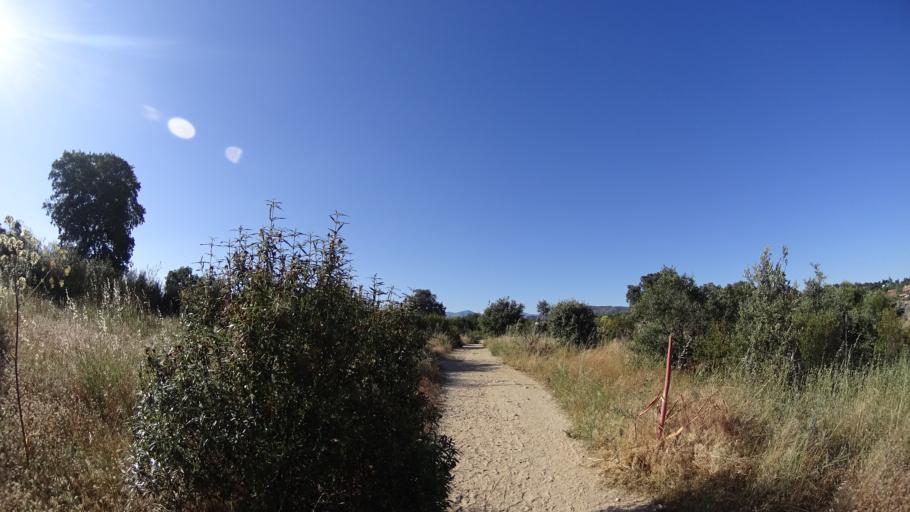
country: ES
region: Madrid
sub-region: Provincia de Madrid
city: Galapagar
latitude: 40.5892
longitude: -3.9736
